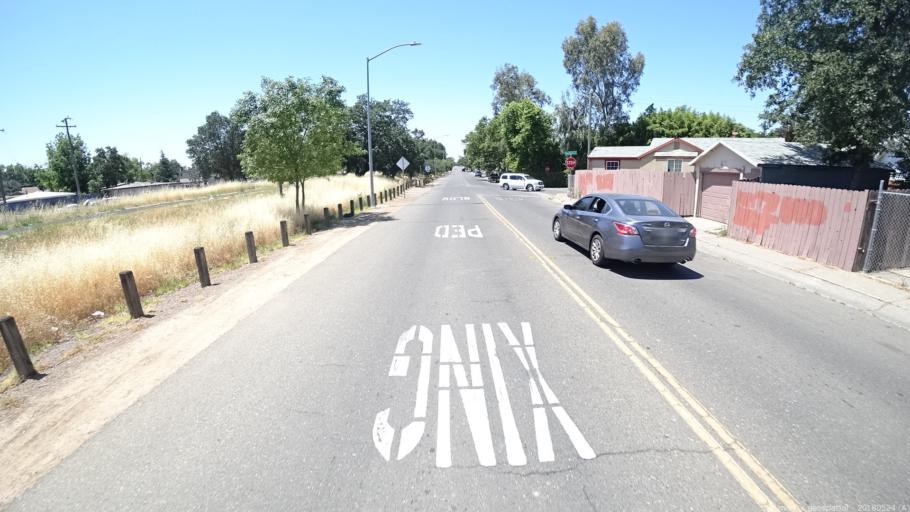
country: US
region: California
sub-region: Sacramento County
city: Sacramento
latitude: 38.6145
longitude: -121.4519
